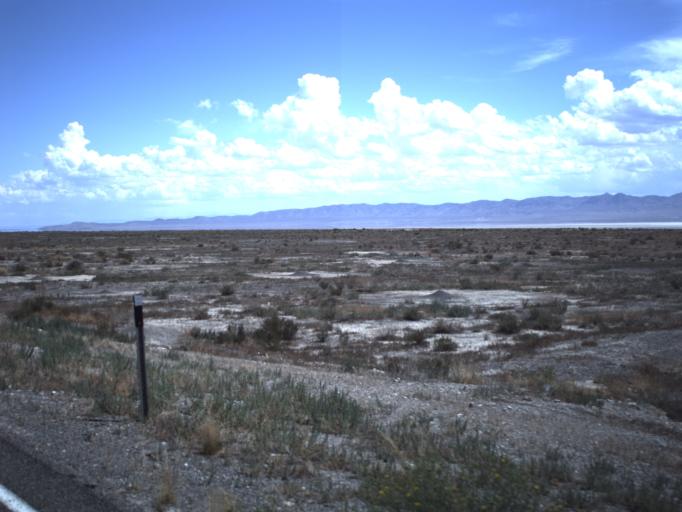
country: US
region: Utah
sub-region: Millard County
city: Delta
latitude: 39.0880
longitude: -113.1787
